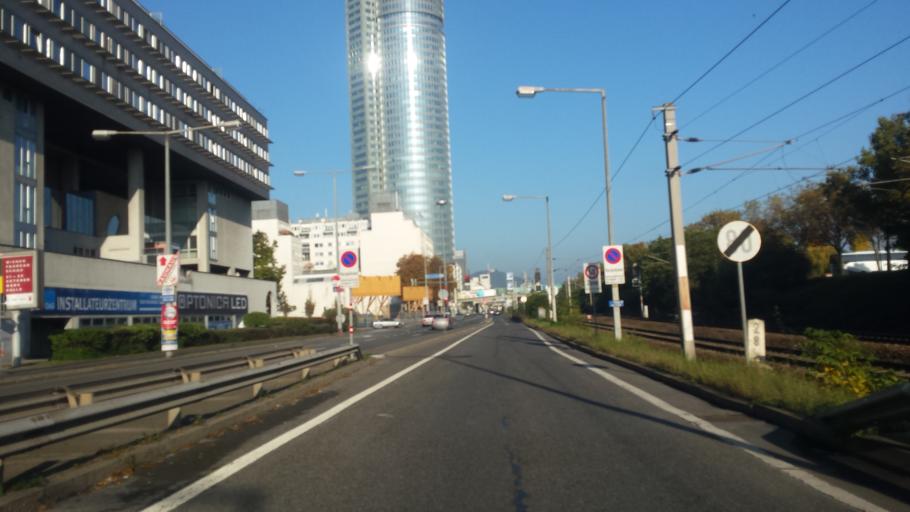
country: AT
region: Vienna
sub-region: Wien Stadt
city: Vienna
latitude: 48.2382
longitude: 16.3899
